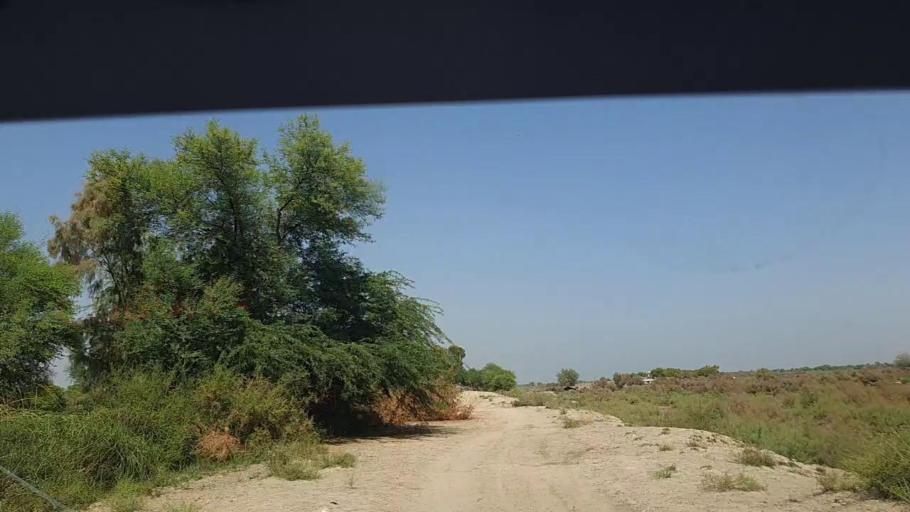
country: PK
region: Sindh
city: Kandhkot
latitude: 28.1779
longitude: 69.1504
